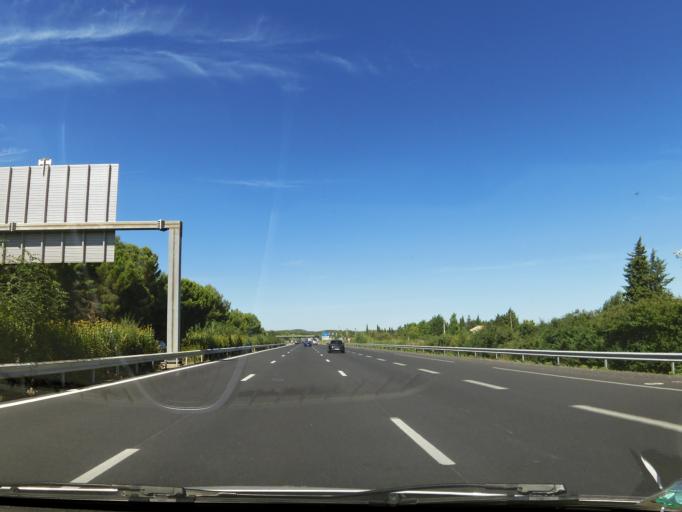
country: FR
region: Languedoc-Roussillon
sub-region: Departement du Gard
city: Marguerittes
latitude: 43.8570
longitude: 4.4267
